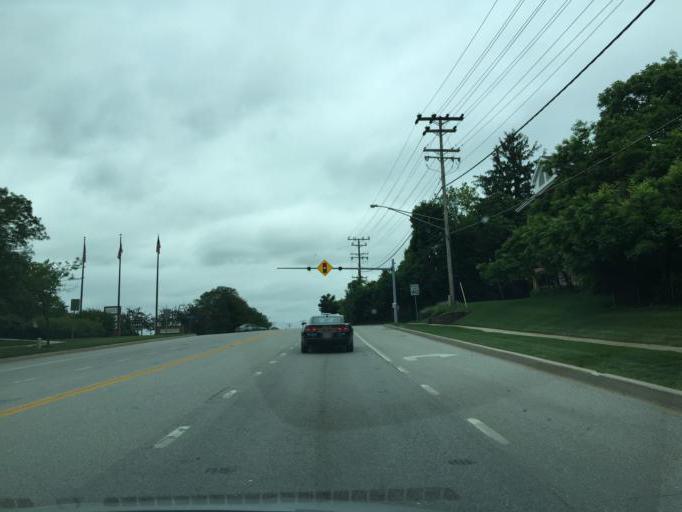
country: US
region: Maryland
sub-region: Baltimore County
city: Hunt Valley
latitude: 39.4979
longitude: -76.6505
